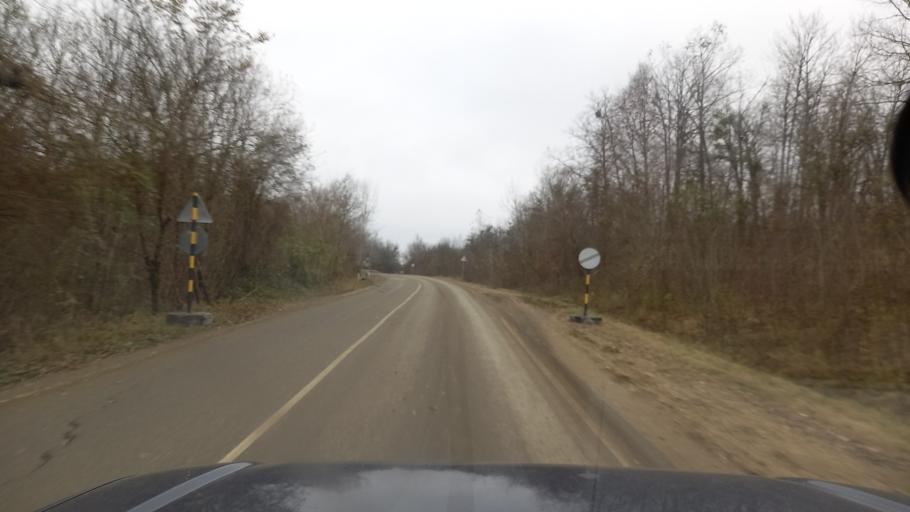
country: RU
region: Krasnodarskiy
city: Goryachiy Klyuch
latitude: 44.5543
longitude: 39.2522
